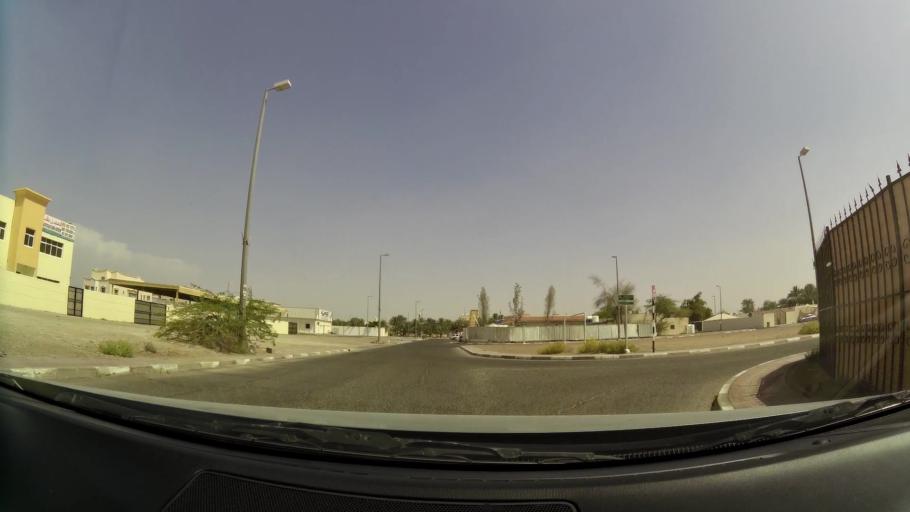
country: AE
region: Abu Dhabi
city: Al Ain
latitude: 24.2300
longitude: 55.7019
